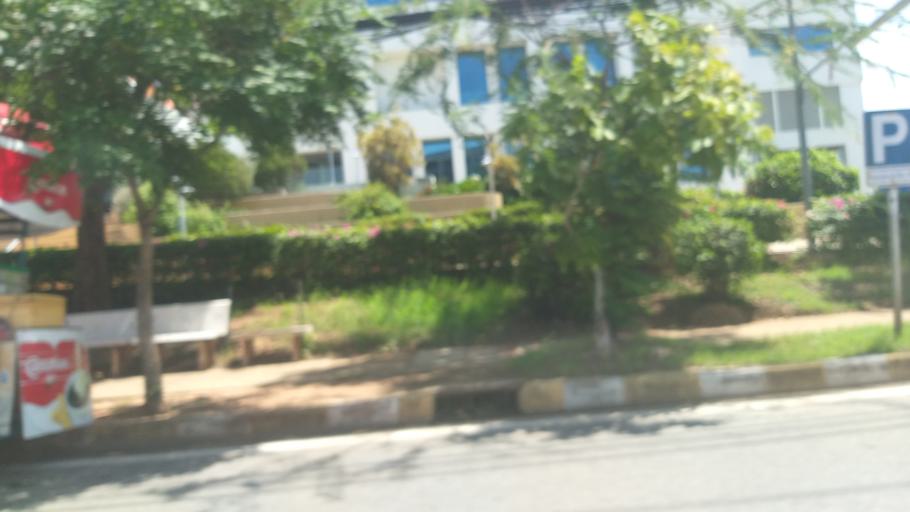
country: TH
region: Khon Kaen
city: Khon Kaen
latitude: 16.4325
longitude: 102.8216
